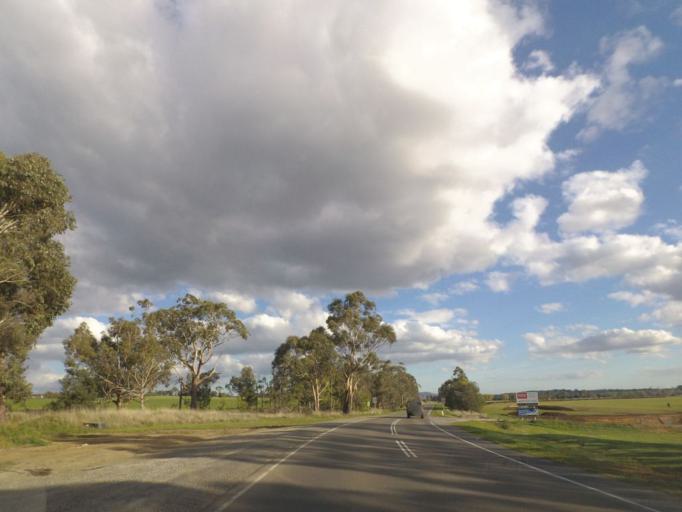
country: AU
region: Victoria
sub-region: Yarra Ranges
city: Yarra Glen
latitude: -37.6944
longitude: 145.3733
